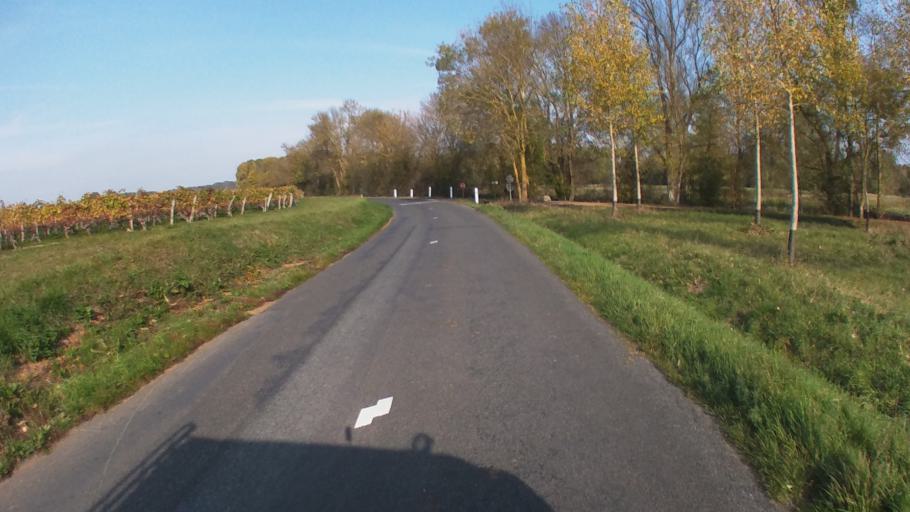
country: FR
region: Pays de la Loire
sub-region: Departement de Maine-et-Loire
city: Chace
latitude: 47.2089
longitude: -0.0898
